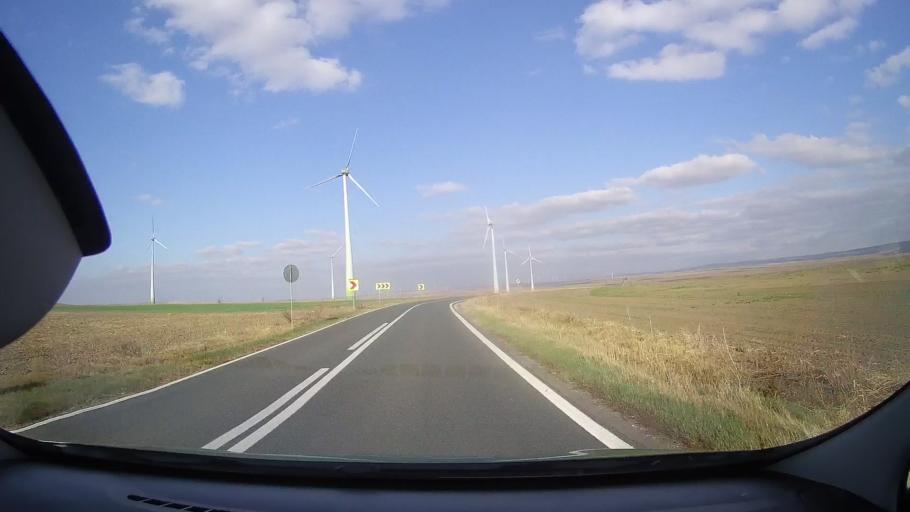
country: RO
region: Tulcea
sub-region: Comuna Topolog
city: Topolog
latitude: 44.8183
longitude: 28.2600
